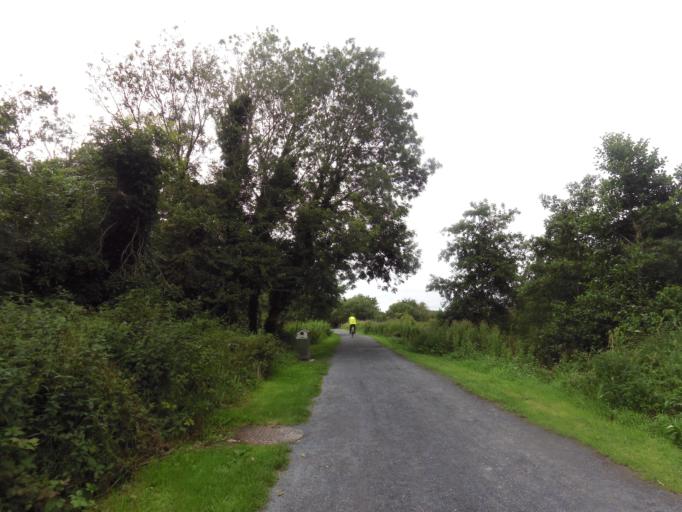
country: IE
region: Connaught
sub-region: County Galway
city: Gaillimh
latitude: 53.2908
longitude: -9.0667
